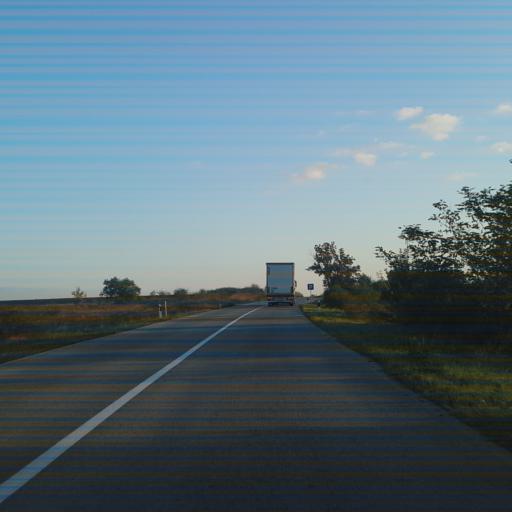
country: RS
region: Central Serbia
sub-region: Zajecarski Okrug
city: Zajecar
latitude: 44.0612
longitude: 22.3333
